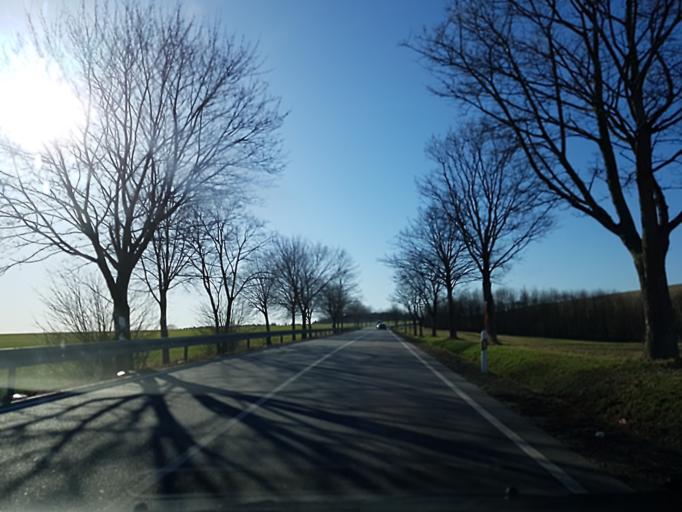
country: DE
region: Saxony
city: Oederan
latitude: 50.8606
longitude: 13.1532
